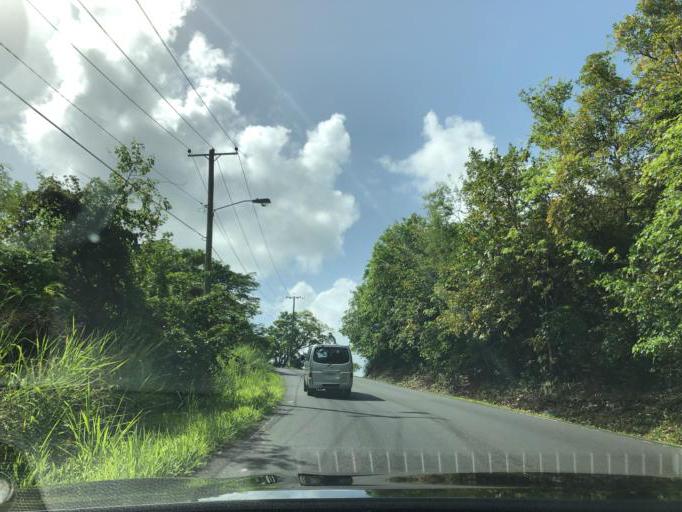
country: LC
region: Dennery Quarter
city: Dennery
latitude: 13.9233
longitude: -60.8959
